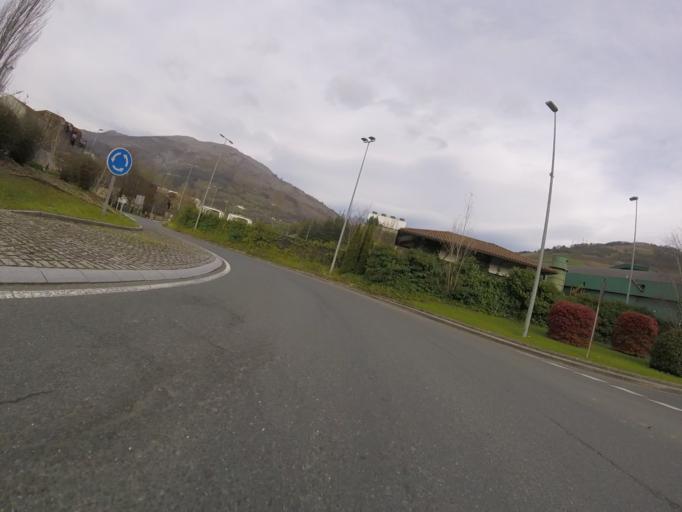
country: ES
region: Basque Country
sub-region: Provincia de Guipuzcoa
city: Azpeitia
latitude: 43.1801
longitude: -2.2591
